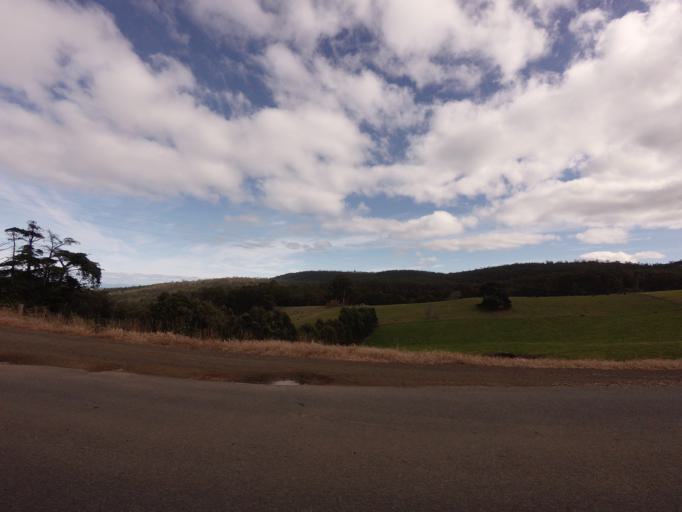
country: AU
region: Tasmania
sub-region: Clarence
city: Sandford
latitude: -43.0699
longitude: 147.7458
